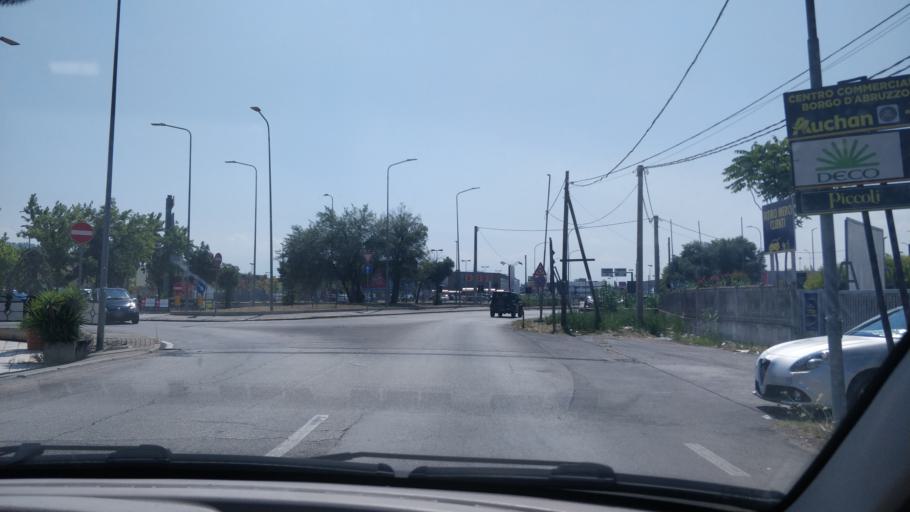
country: IT
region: Abruzzo
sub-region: Provincia di Chieti
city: Sambuceto
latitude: 42.4167
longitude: 14.1719
